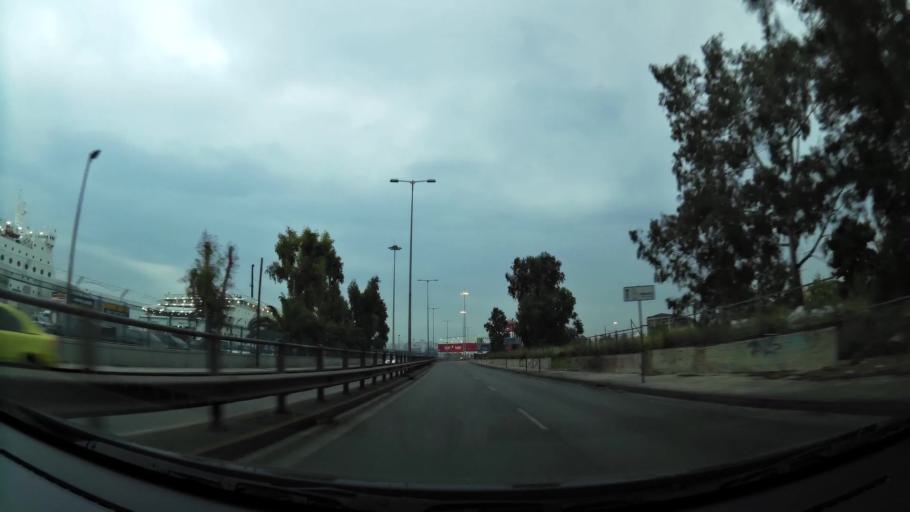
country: GR
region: Attica
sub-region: Nomos Attikis
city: Piraeus
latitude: 37.9477
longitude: 23.6360
